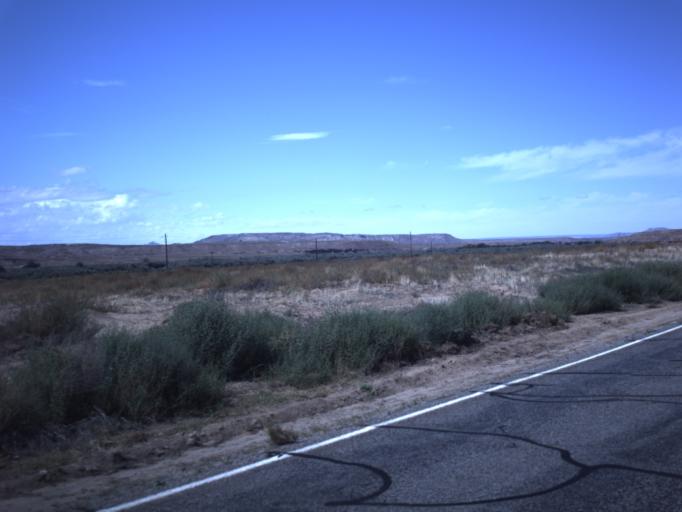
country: US
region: Utah
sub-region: San Juan County
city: Blanding
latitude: 37.2293
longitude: -109.2138
